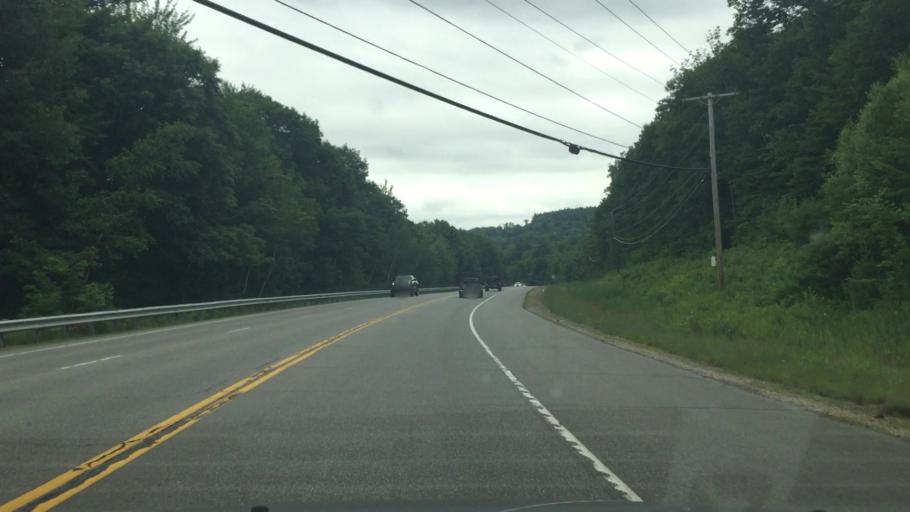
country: US
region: New Hampshire
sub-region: Belknap County
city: Meredith
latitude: 43.6425
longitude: -71.5191
